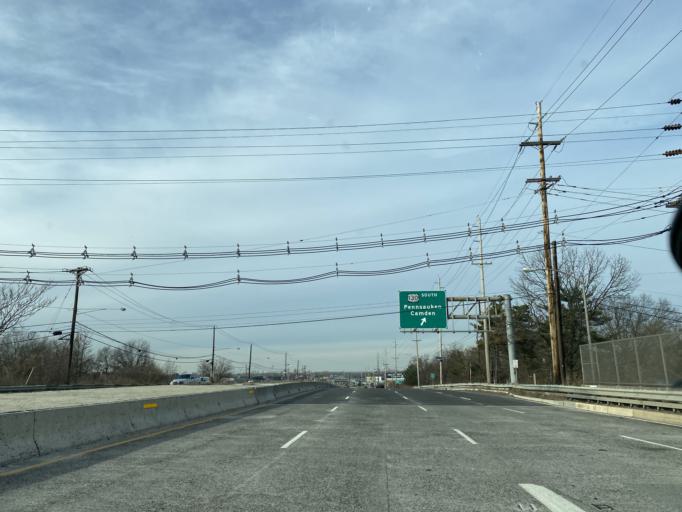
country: US
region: New Jersey
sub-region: Burlington County
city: Palmyra
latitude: 39.9838
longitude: -75.0177
